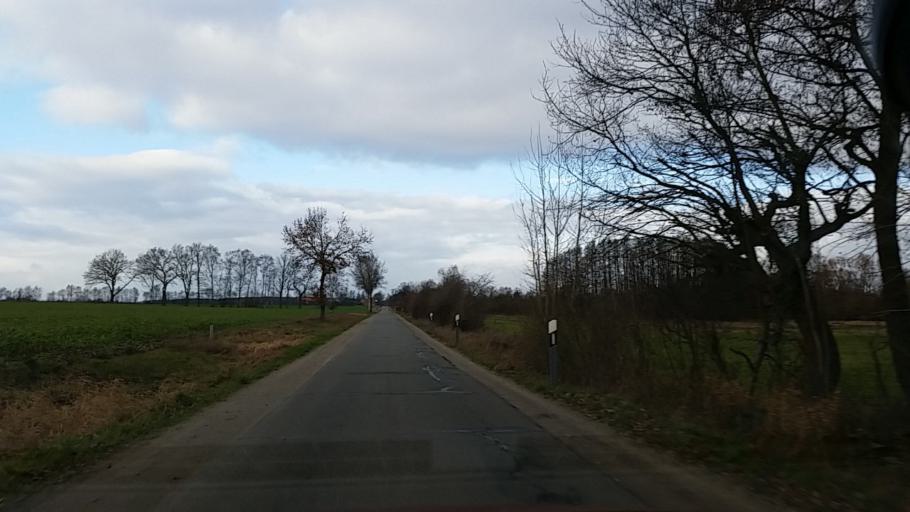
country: DE
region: Lower Saxony
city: Wieren
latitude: 52.8736
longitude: 10.6581
